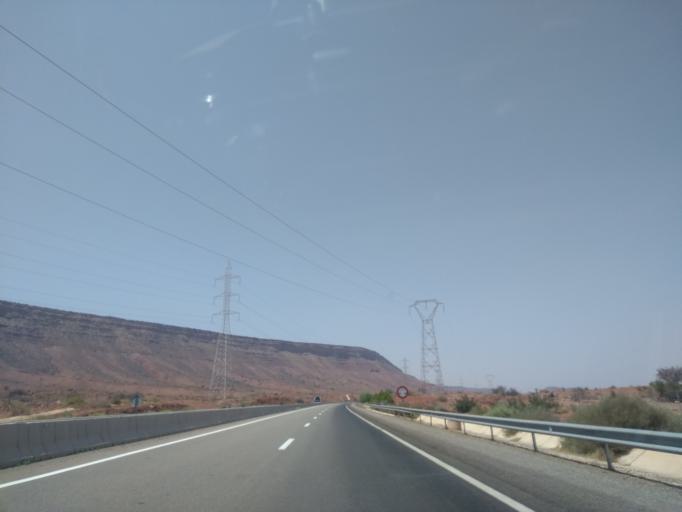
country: MA
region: Marrakech-Tensift-Al Haouz
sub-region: Chichaoua
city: Timezgadiouine
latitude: 30.9184
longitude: -9.0707
